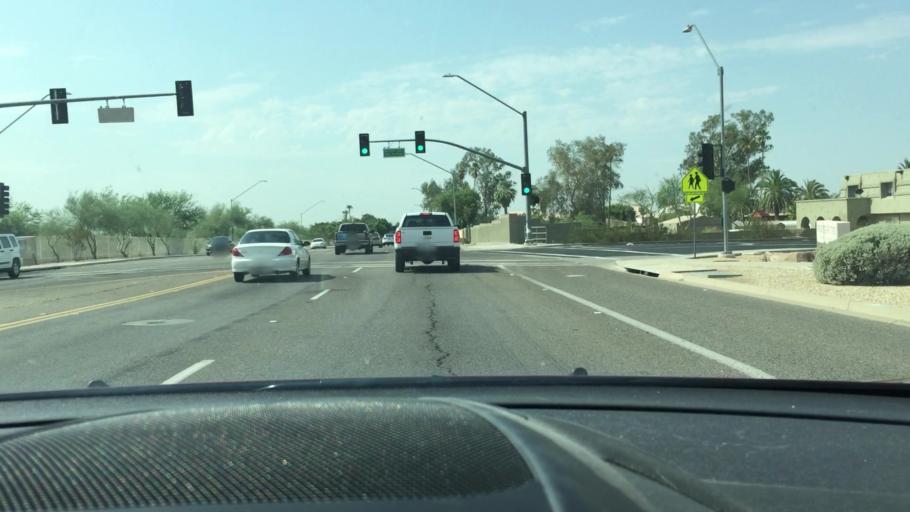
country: US
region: Arizona
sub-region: Maricopa County
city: Peoria
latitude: 33.6895
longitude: -112.2032
